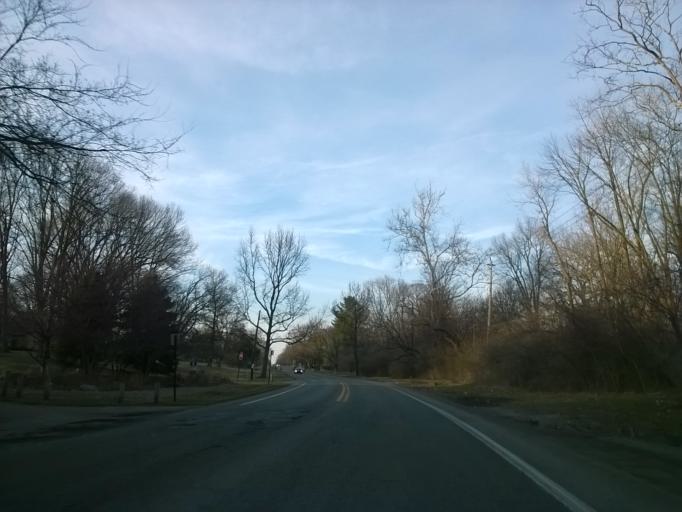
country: US
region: Indiana
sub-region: Marion County
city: Speedway
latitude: 39.8380
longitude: -86.2118
